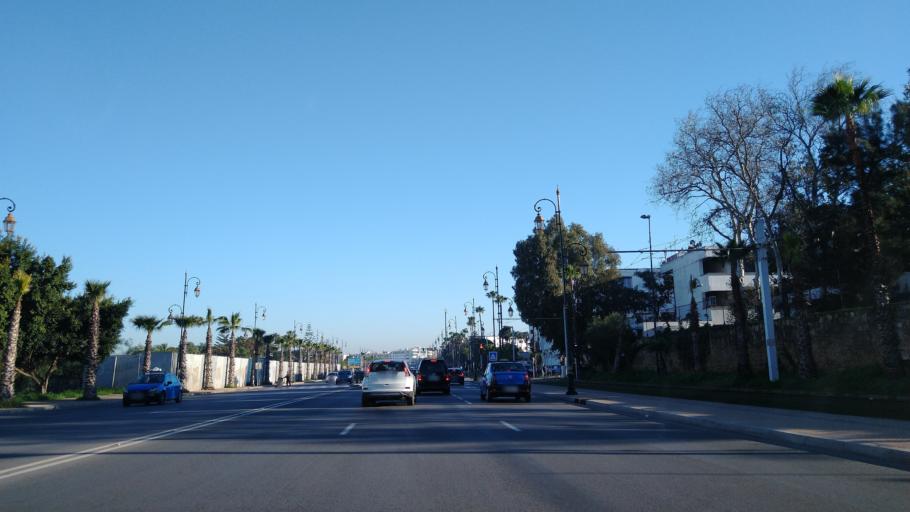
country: MA
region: Rabat-Sale-Zemmour-Zaer
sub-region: Rabat
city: Rabat
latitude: 33.9918
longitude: -6.8555
